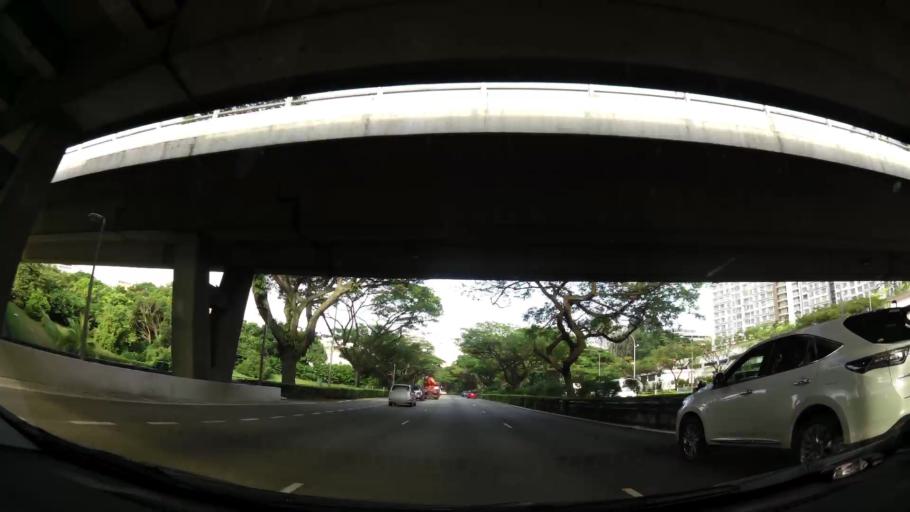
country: SG
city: Singapore
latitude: 1.3436
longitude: 103.7451
